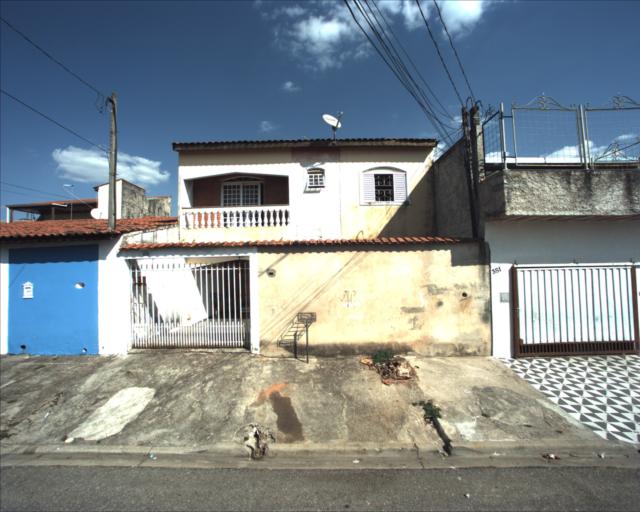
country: BR
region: Sao Paulo
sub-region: Sorocaba
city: Sorocaba
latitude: -23.4991
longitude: -47.5176
